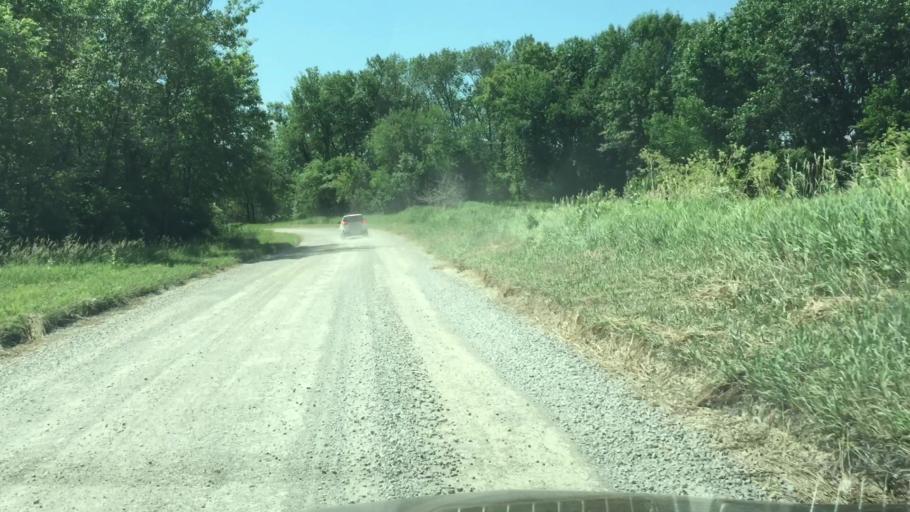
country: US
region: Iowa
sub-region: Linn County
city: Ely
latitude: 41.8194
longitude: -91.5894
